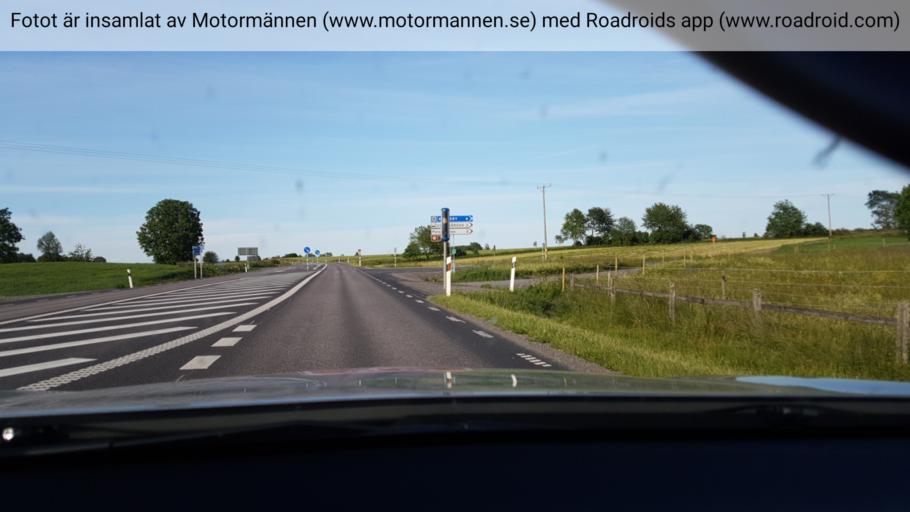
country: SE
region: Vaestra Goetaland
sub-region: Falkopings Kommun
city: Akarp
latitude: 58.2002
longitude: 13.6140
